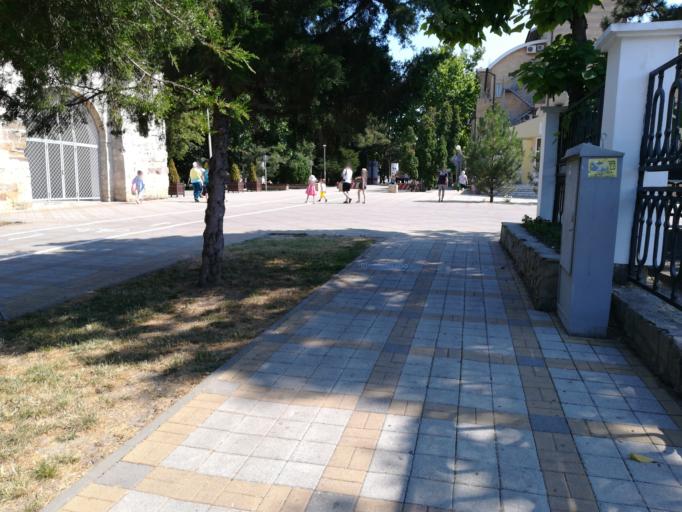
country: RU
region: Krasnodarskiy
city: Anapa
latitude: 44.8958
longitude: 37.3112
